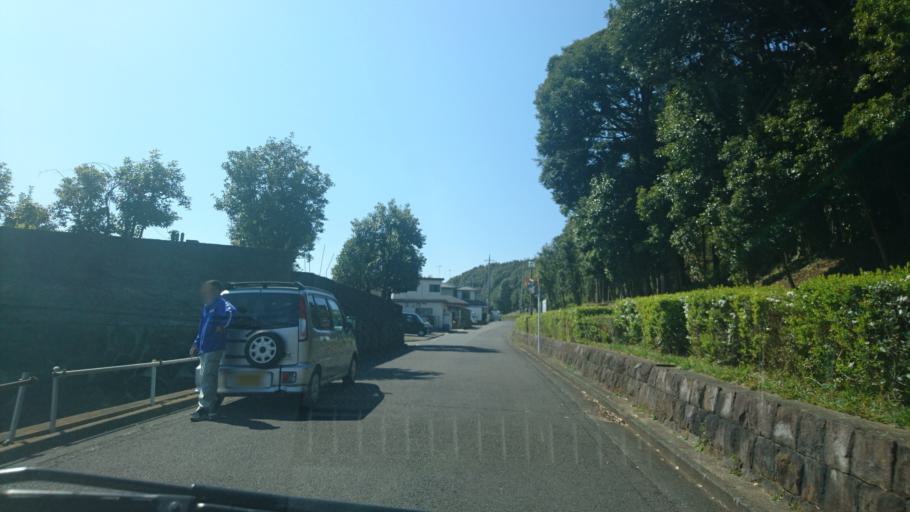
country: JP
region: Kanagawa
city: Fujisawa
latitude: 35.3887
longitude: 139.4317
